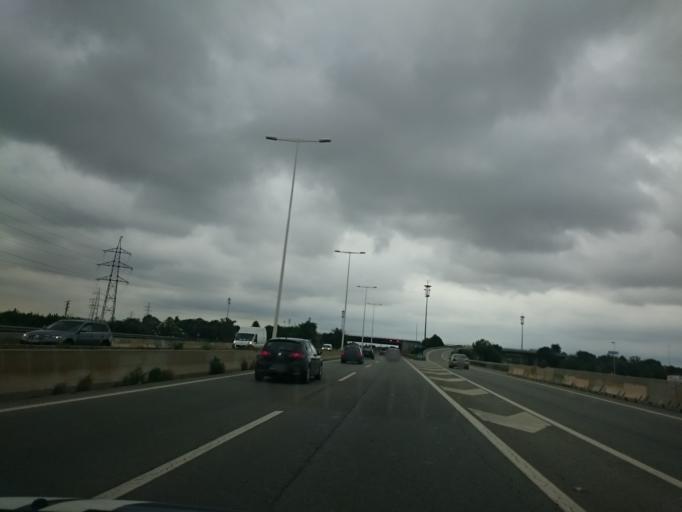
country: ES
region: Catalonia
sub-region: Provincia de Barcelona
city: Cornella de Llobregat
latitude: 41.3329
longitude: 2.0661
